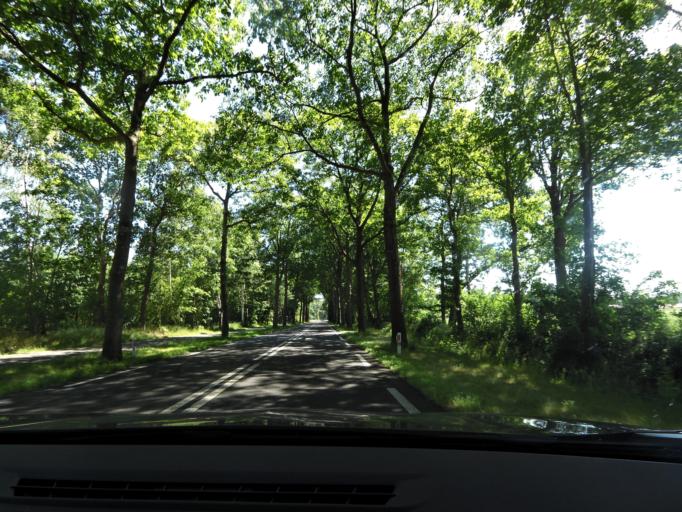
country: NL
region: Gelderland
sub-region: Berkelland
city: Neede
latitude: 52.1561
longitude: 6.6038
